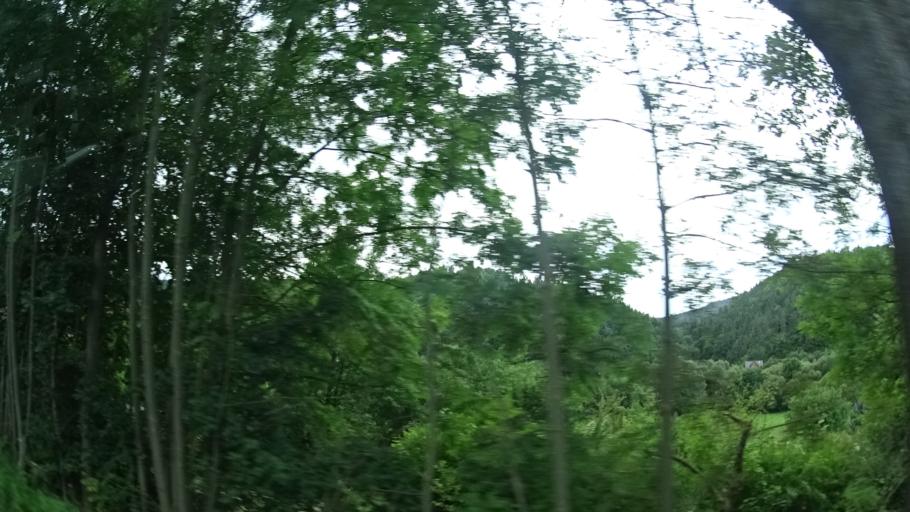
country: DE
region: Thuringia
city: Saalfeld
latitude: 50.6249
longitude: 11.3831
